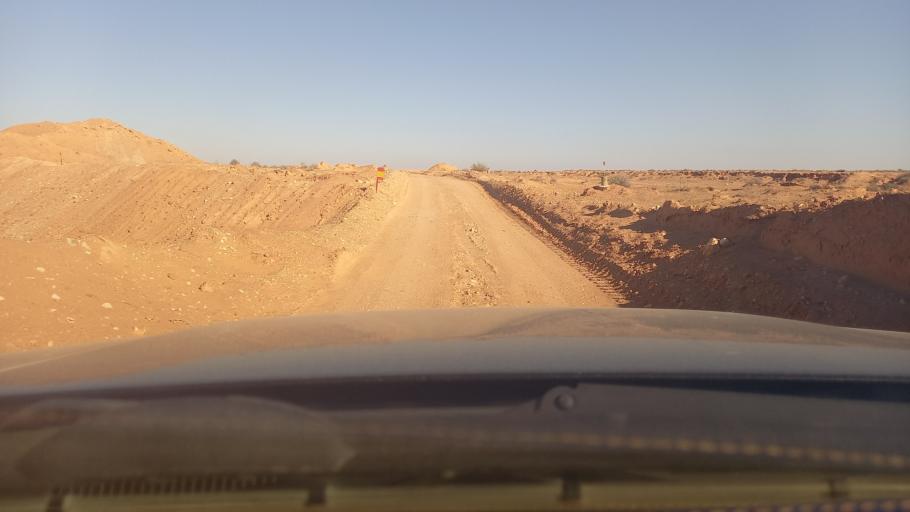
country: TN
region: Madanin
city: Medenine
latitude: 33.1479
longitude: 10.5074
